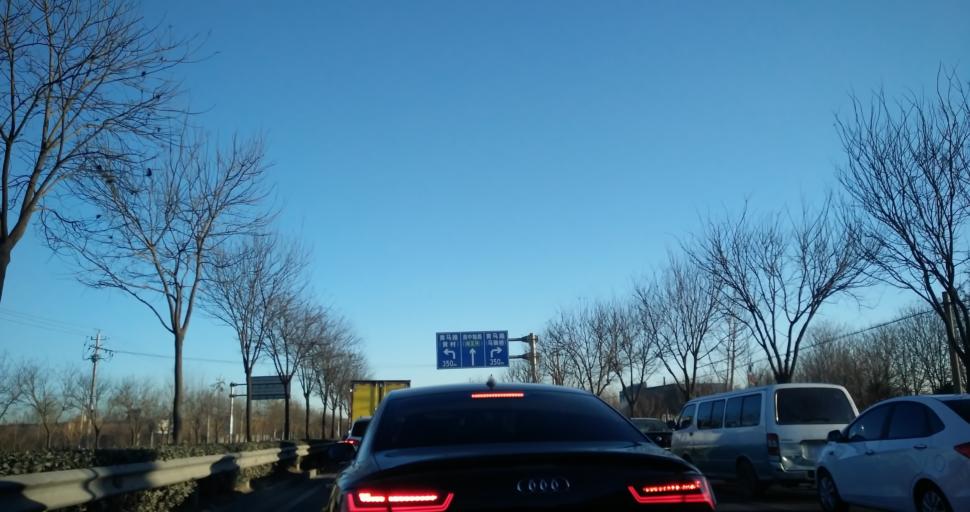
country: CN
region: Beijing
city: Yinghai
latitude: 39.7156
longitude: 116.4027
